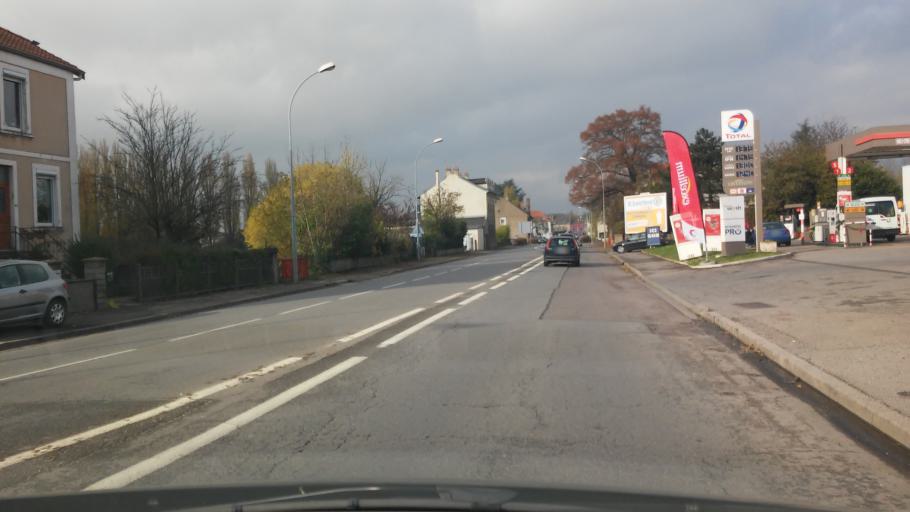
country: FR
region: Lorraine
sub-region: Departement de la Moselle
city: Uckange
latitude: 49.2973
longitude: 6.1648
